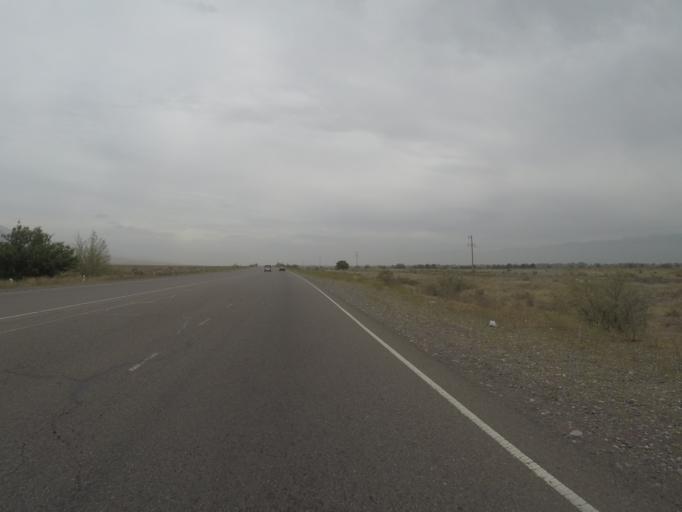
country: KG
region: Chuy
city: Tokmok
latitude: 42.8302
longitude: 75.4623
